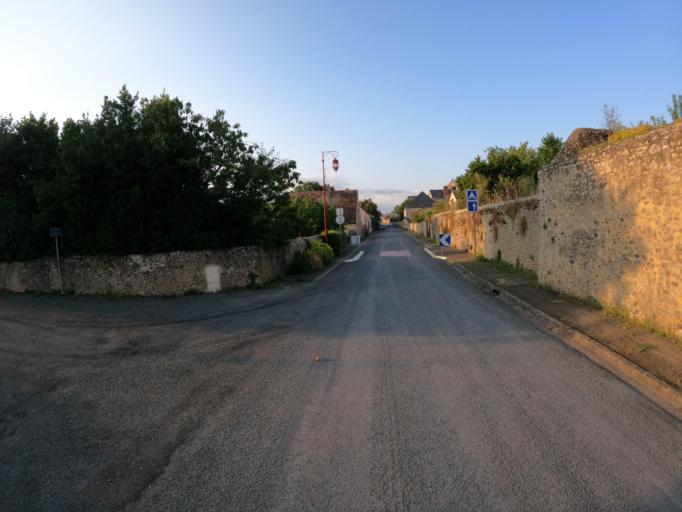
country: FR
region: Pays de la Loire
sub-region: Departement de la Sarthe
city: Parce-sur-Sarthe
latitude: 47.9029
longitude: -0.2220
